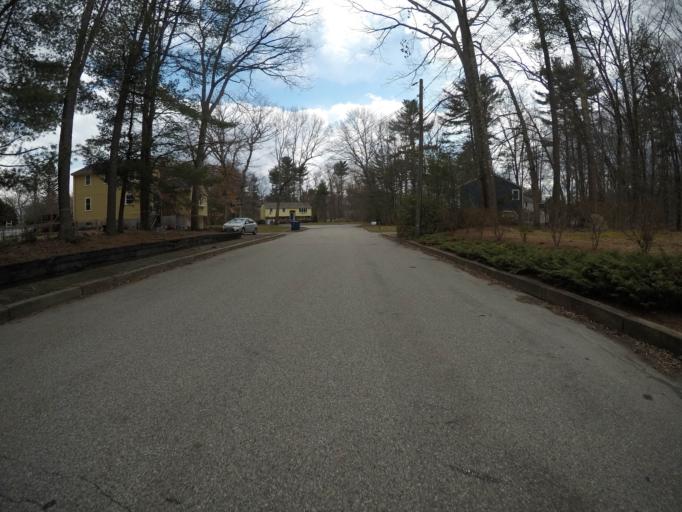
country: US
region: Massachusetts
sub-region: Bristol County
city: Easton
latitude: 42.0499
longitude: -71.1351
